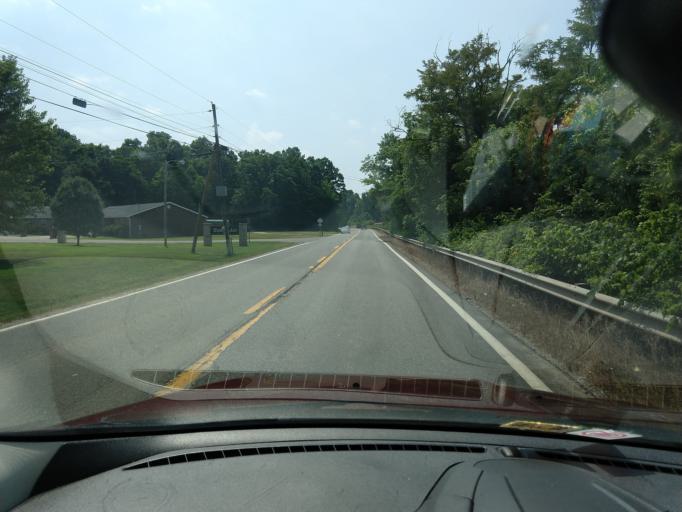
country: US
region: West Virginia
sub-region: Jackson County
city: Ripley
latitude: 38.8347
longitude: -81.7769
